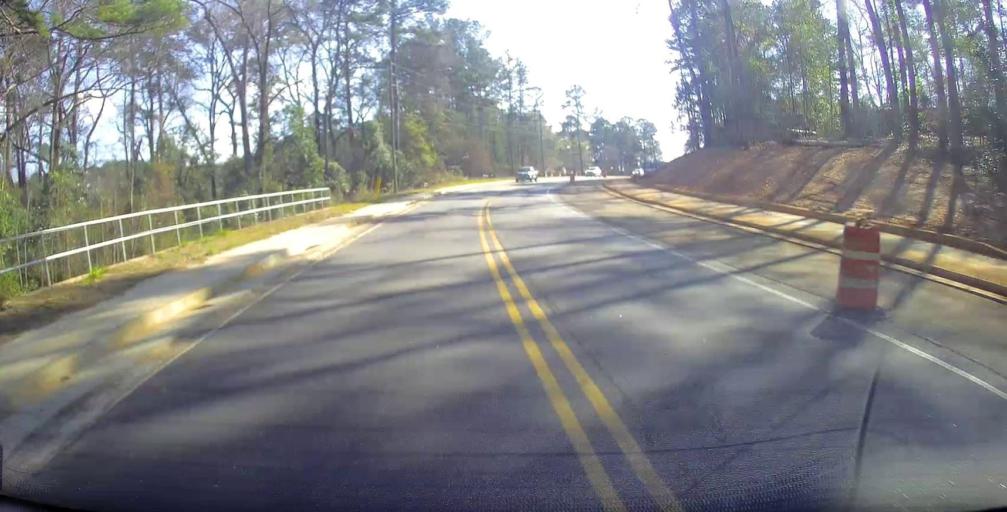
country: US
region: Georgia
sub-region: Laurens County
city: Dublin
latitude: 32.5377
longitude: -82.9480
